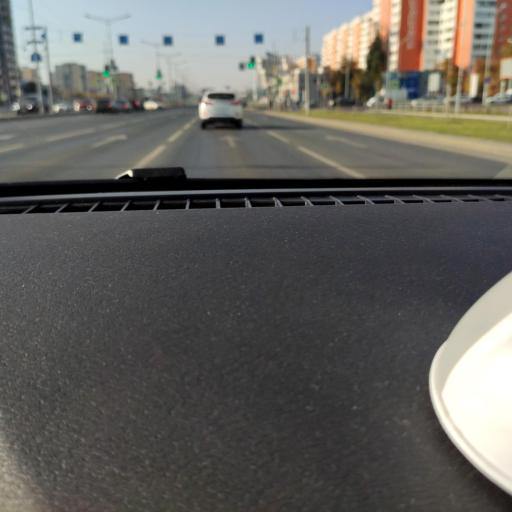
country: RU
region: Samara
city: Samara
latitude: 53.2564
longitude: 50.2313
